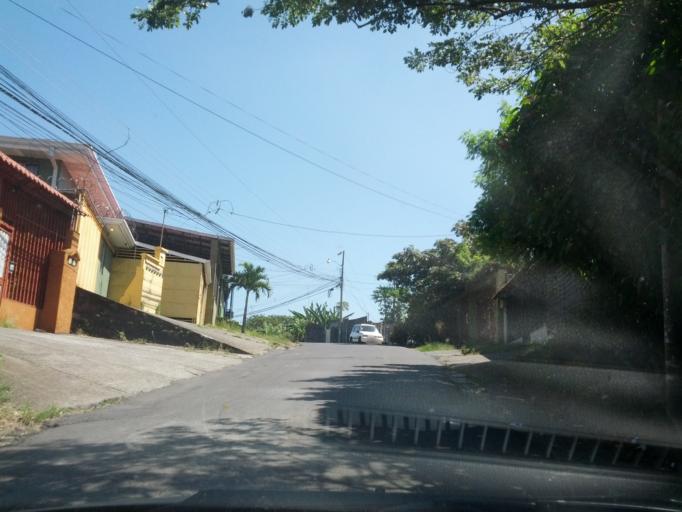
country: CR
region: Alajuela
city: Alajuela
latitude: 10.0084
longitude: -84.1978
